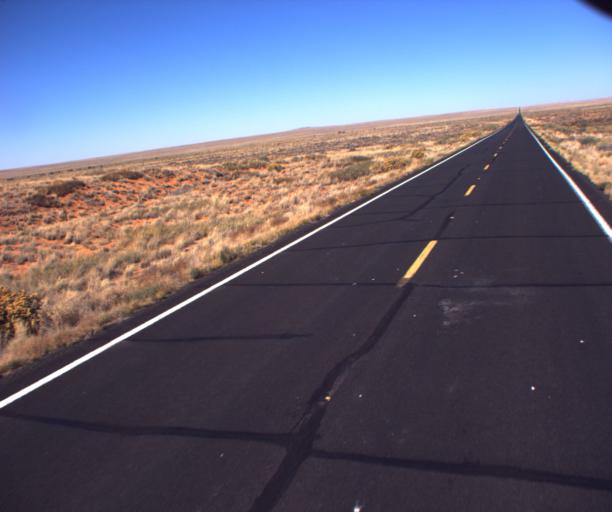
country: US
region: Arizona
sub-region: Navajo County
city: Dilkon
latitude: 35.5636
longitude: -110.4575
